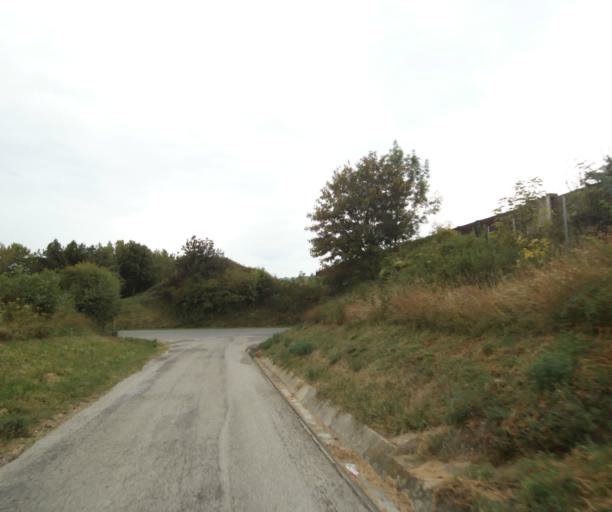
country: FR
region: Bourgogne
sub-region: Departement de Saone-et-Loire
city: Tournus
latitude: 46.5723
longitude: 4.8971
